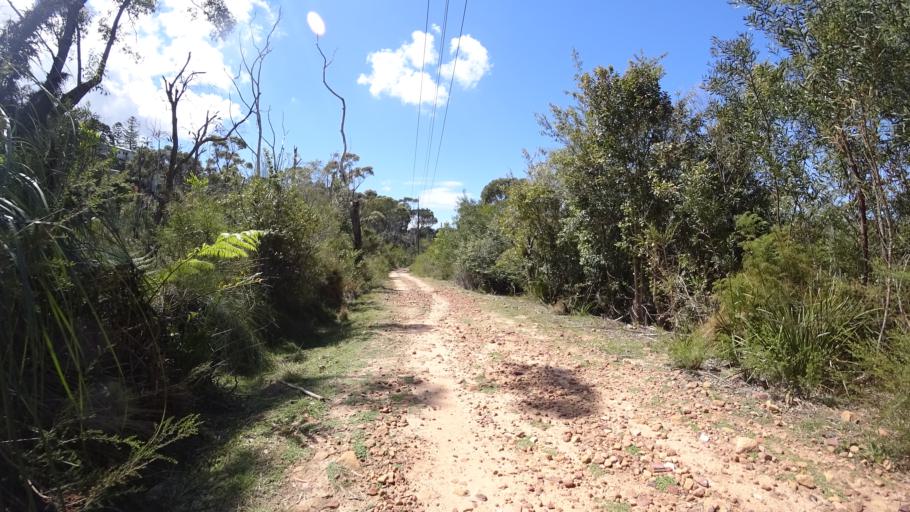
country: AU
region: New South Wales
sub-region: Warringah
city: Killarney Heights
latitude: -33.7625
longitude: 151.2223
